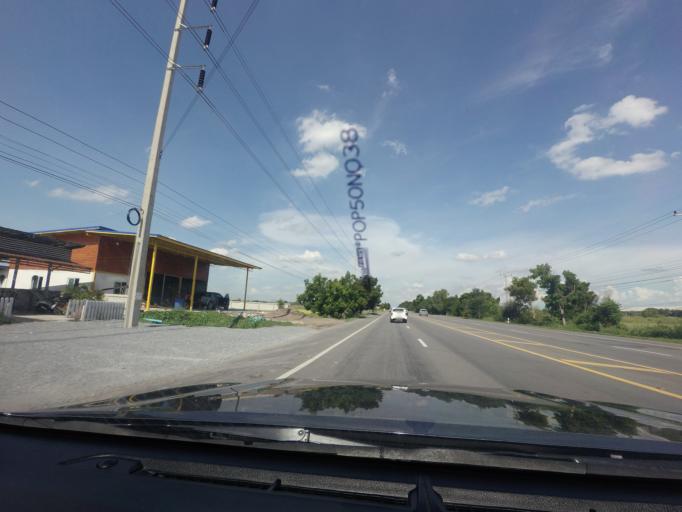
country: TH
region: Phra Nakhon Si Ayutthaya
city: Lat Bua Luang
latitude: 14.1601
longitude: 100.2299
